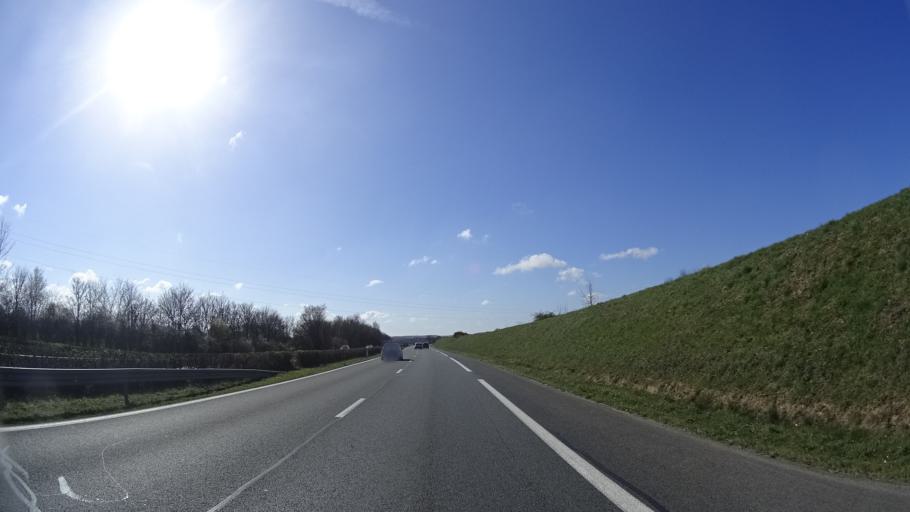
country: FR
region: Pays de la Loire
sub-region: Departement de Maine-et-Loire
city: Avrille
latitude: 47.5096
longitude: -0.6185
